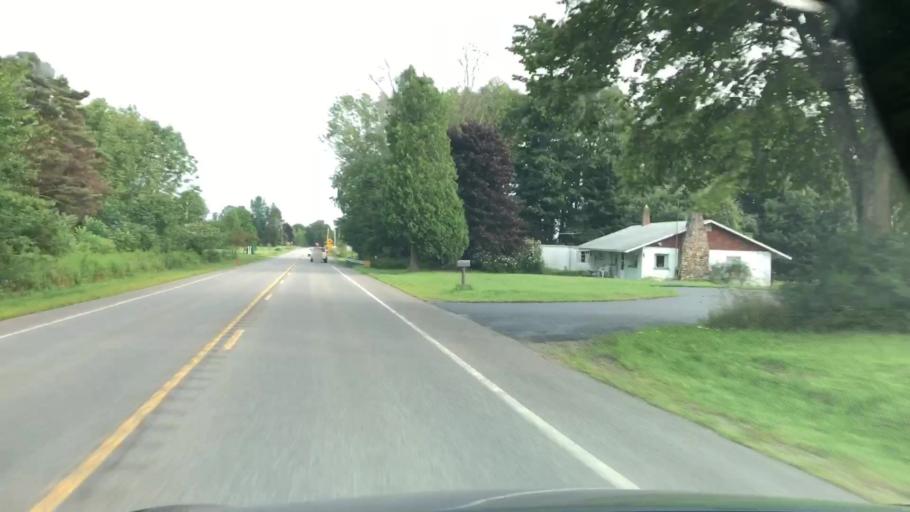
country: US
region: Pennsylvania
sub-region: Erie County
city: Union City
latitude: 41.8238
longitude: -79.8099
